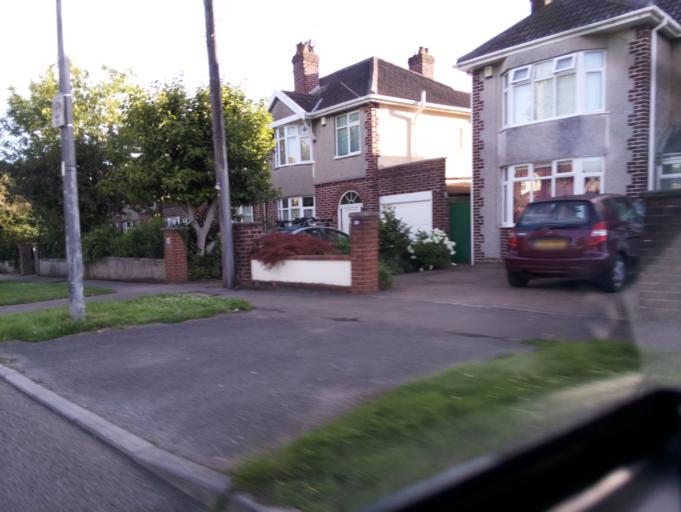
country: GB
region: England
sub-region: South Gloucestershire
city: Mangotsfield
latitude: 51.4951
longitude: -2.5121
